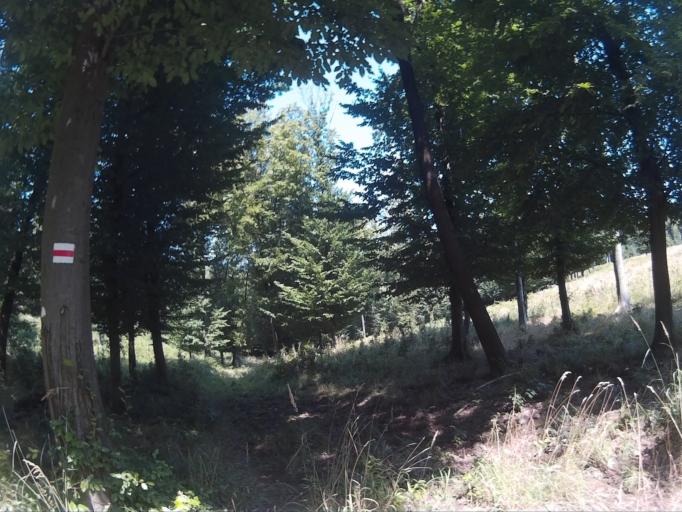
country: HU
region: Veszprem
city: Zirc
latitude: 47.1911
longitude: 17.8792
